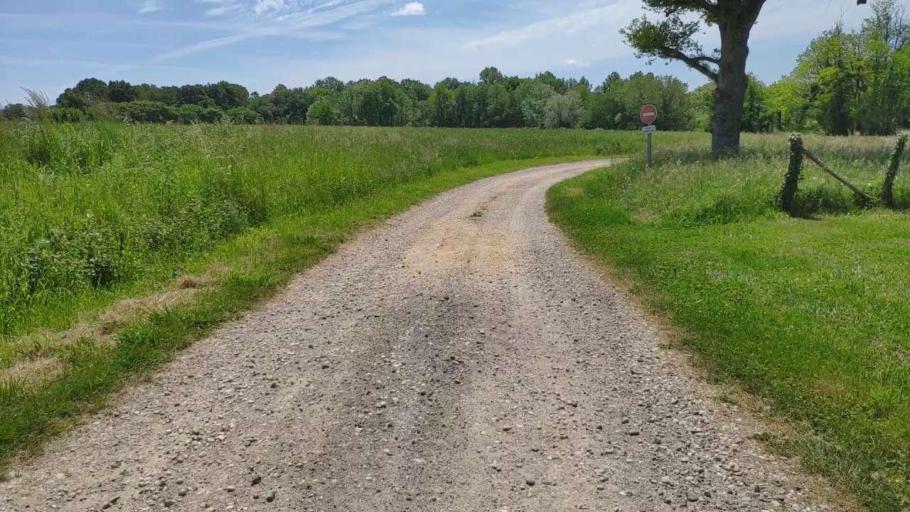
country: FR
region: Franche-Comte
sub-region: Departement du Jura
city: Bletterans
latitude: 46.7874
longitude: 5.3683
